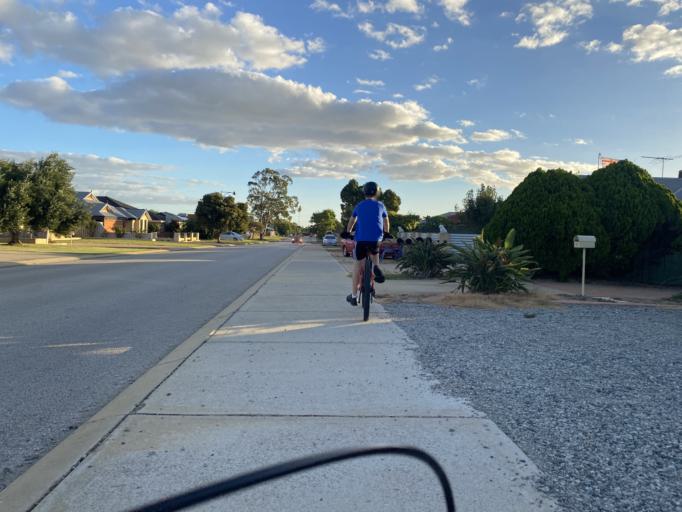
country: AU
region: Western Australia
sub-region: Kalamunda
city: Maida Vale
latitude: -31.9704
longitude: 116.0055
